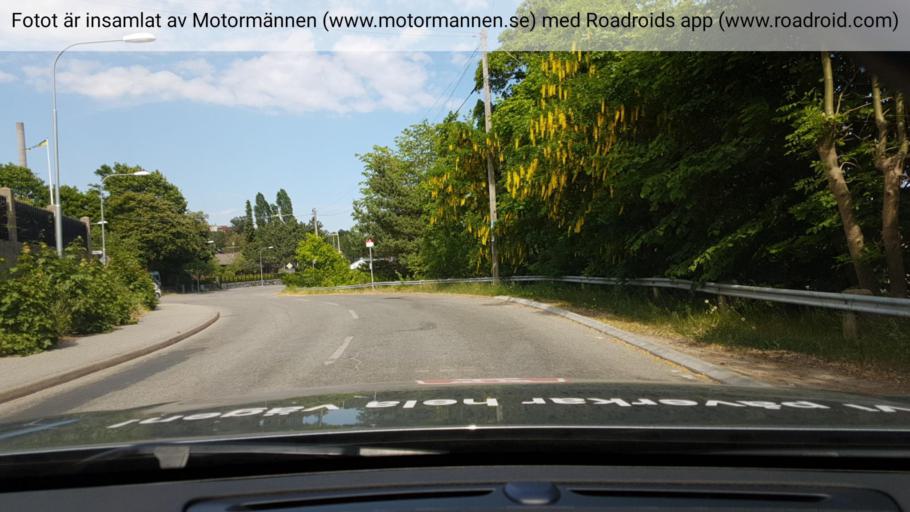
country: SE
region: Stockholm
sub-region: Lidingo
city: Brevik
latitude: 59.3484
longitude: 18.2229
